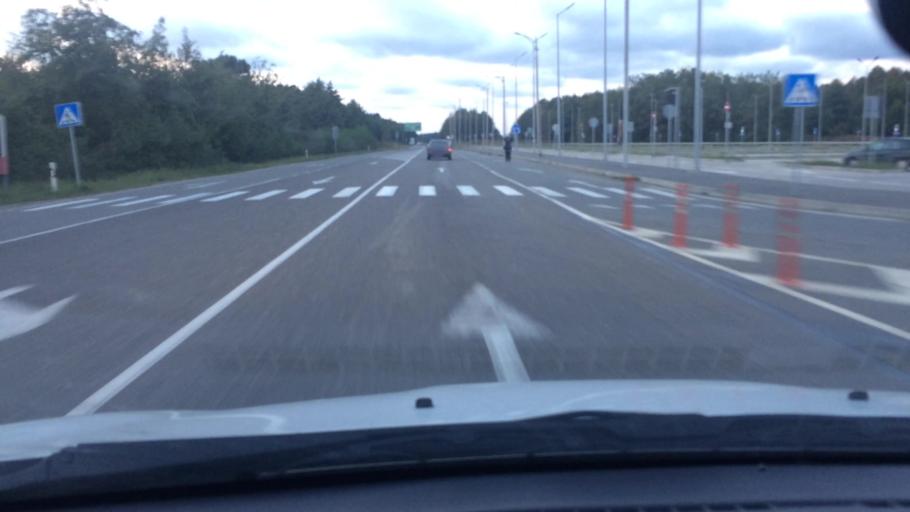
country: GE
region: Guria
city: Urek'i
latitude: 41.9388
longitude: 41.7714
